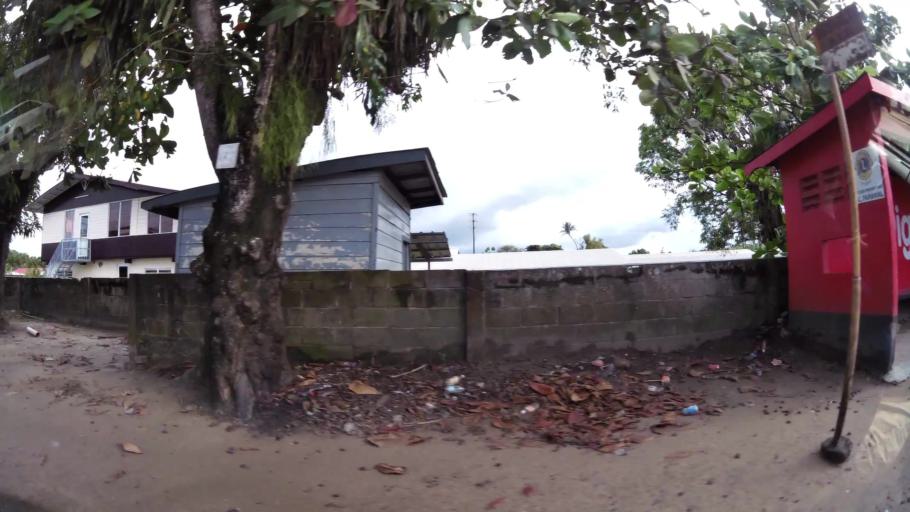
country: SR
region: Paramaribo
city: Paramaribo
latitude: 5.8464
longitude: -55.2319
